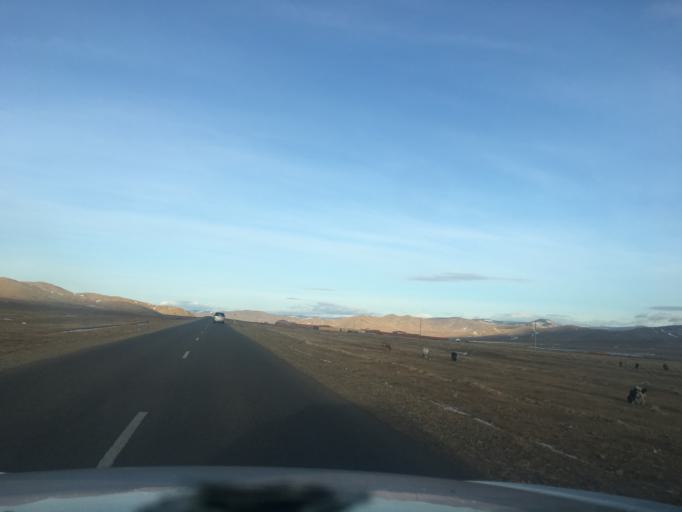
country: MN
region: Central Aimak
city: Mandal
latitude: 48.0972
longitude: 106.6140
